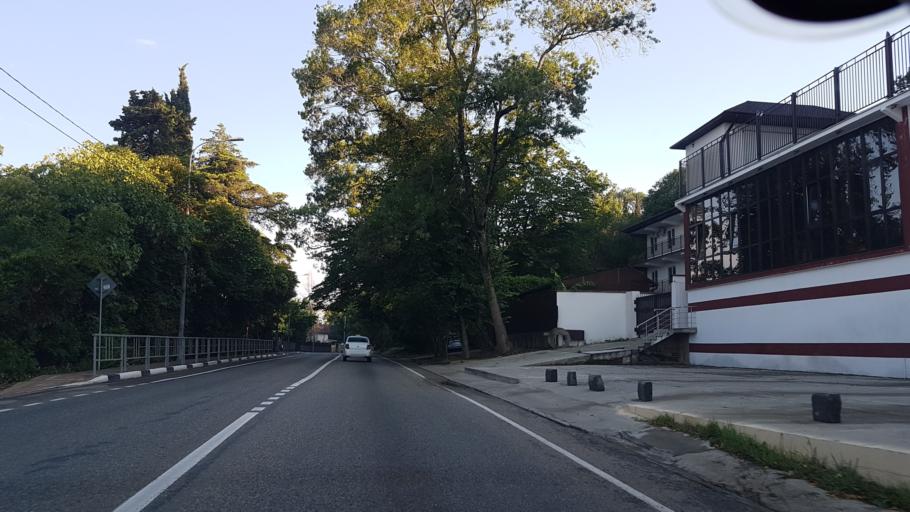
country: RU
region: Krasnodarskiy
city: Gornoye Loo
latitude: 43.6830
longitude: 39.5994
